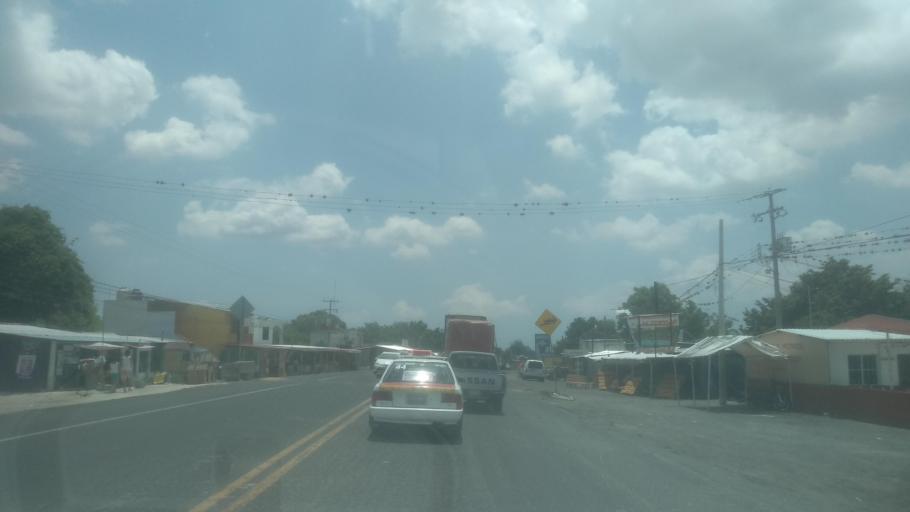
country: MX
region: Veracruz
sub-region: Emiliano Zapata
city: Plan del Rio
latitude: 19.3915
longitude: -96.6353
